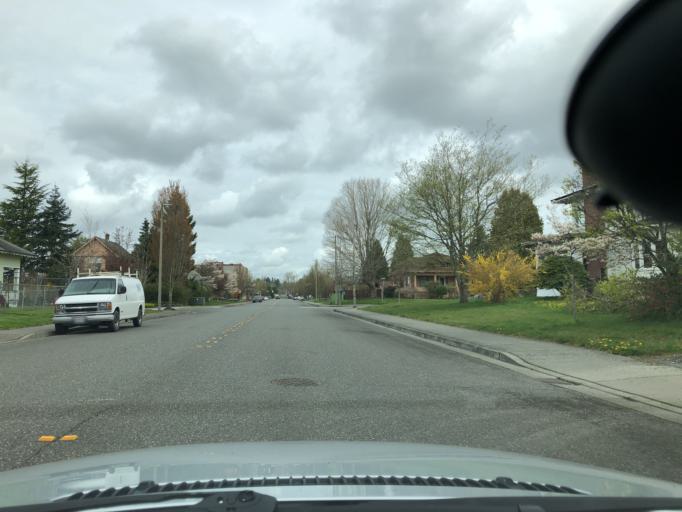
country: US
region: Washington
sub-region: Whatcom County
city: Blaine
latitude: 48.9916
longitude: -122.7498
